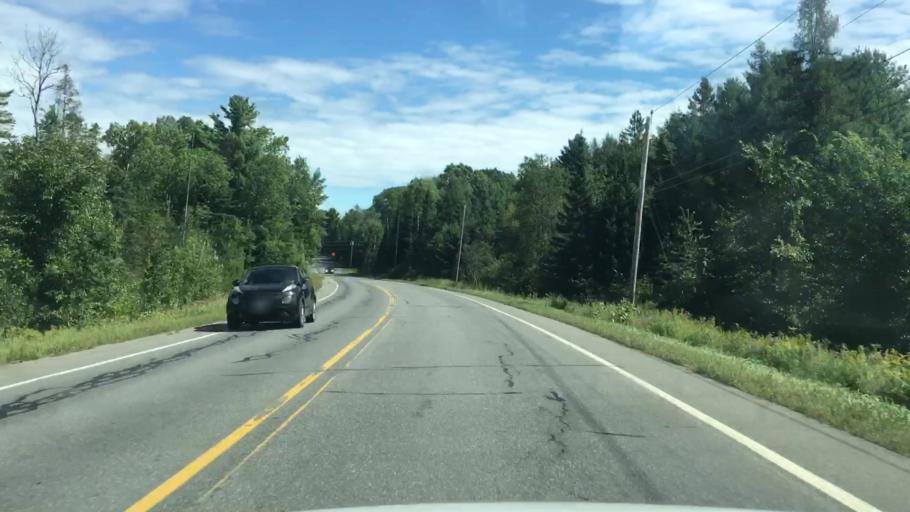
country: US
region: Maine
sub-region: Penobscot County
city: Garland
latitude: 45.0918
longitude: -69.2141
